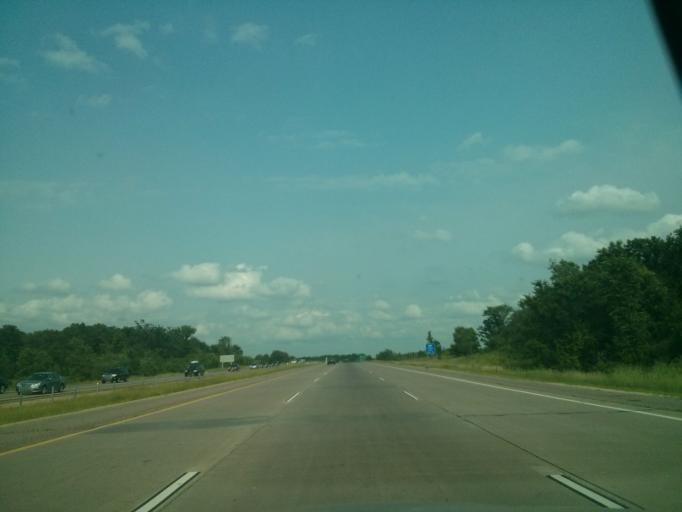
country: US
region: Wisconsin
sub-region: Saint Croix County
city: Hudson
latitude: 44.9649
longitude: -92.6679
